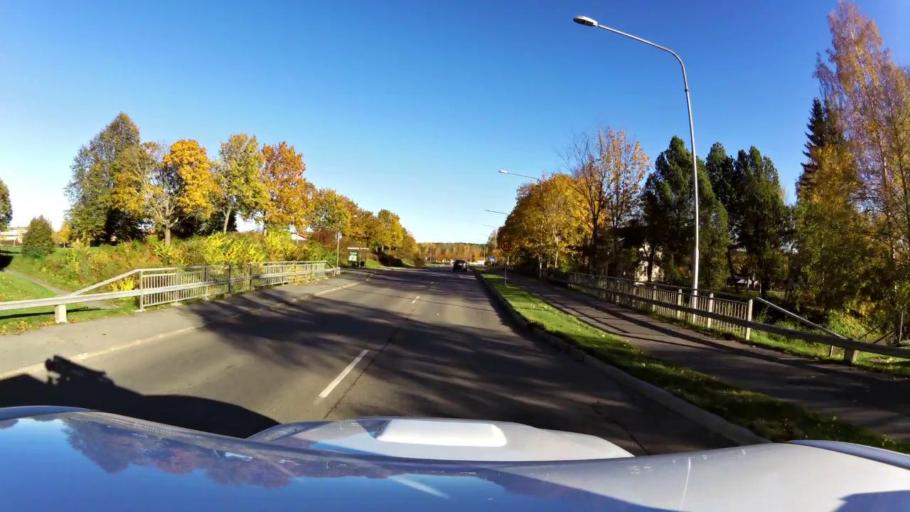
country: SE
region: OEstergoetland
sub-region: Linkopings Kommun
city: Ljungsbro
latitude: 58.5045
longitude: 15.5074
